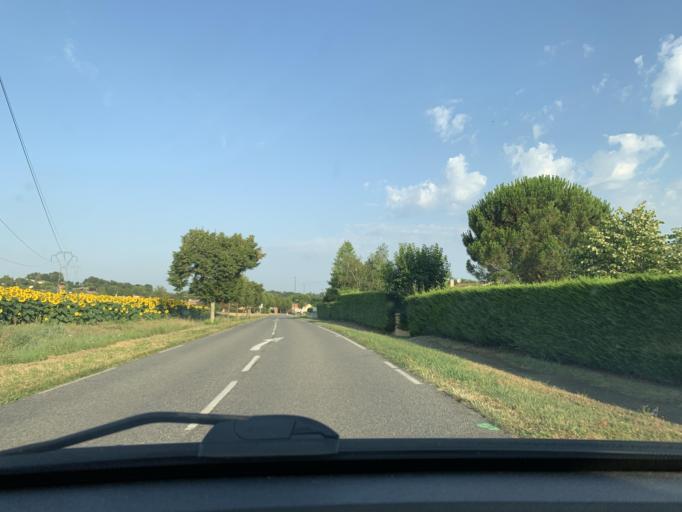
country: FR
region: Midi-Pyrenees
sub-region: Departement de la Haute-Garonne
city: Escalquens
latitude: 43.5292
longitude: 1.5571
